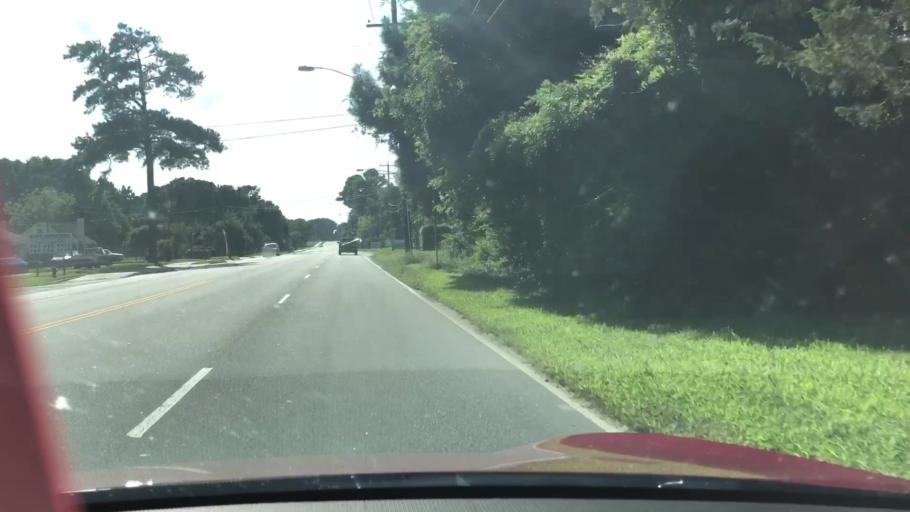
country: US
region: Virginia
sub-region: City of Virginia Beach
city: Virginia Beach
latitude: 36.8427
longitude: -76.0056
